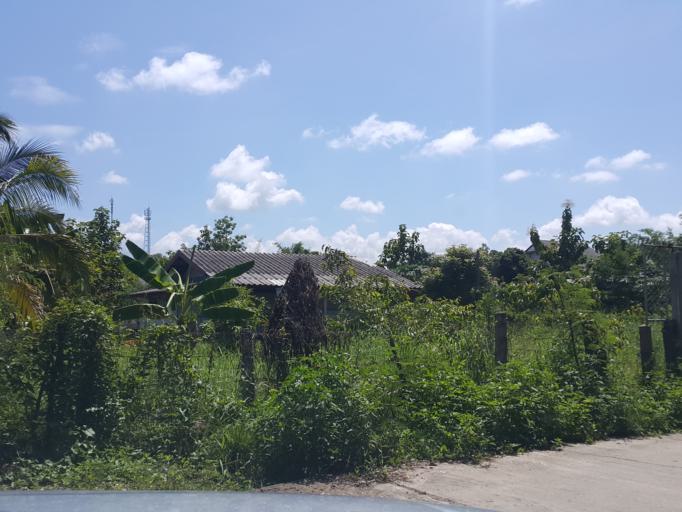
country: TH
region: Chiang Mai
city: San Kamphaeng
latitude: 18.7164
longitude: 99.1067
